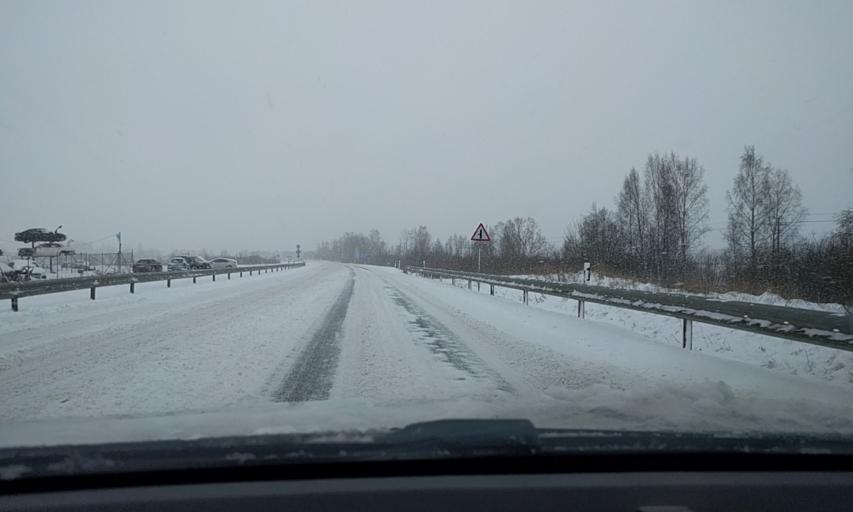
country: EE
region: Harju
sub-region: Joelaehtme vald
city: Loo
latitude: 59.4651
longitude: 24.9798
